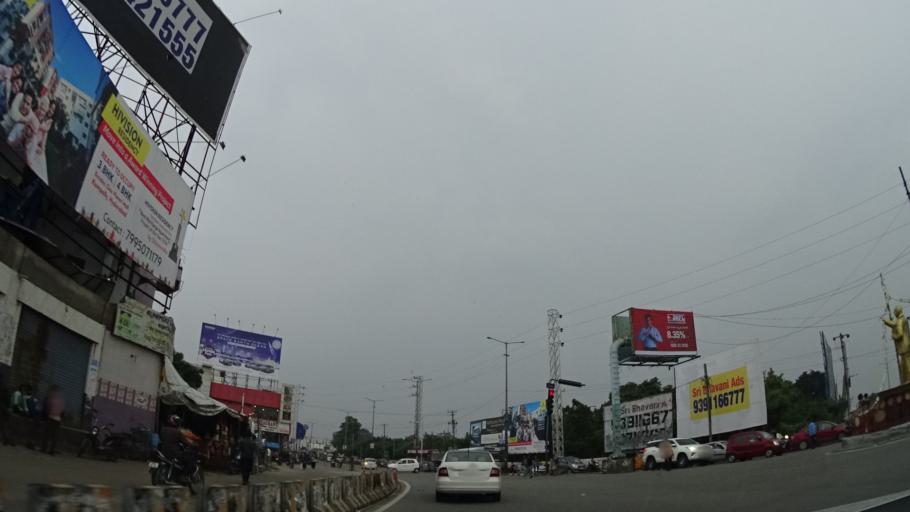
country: IN
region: Telangana
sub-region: Rangareddi
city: Quthbullapur
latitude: 17.4641
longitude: 78.4728
